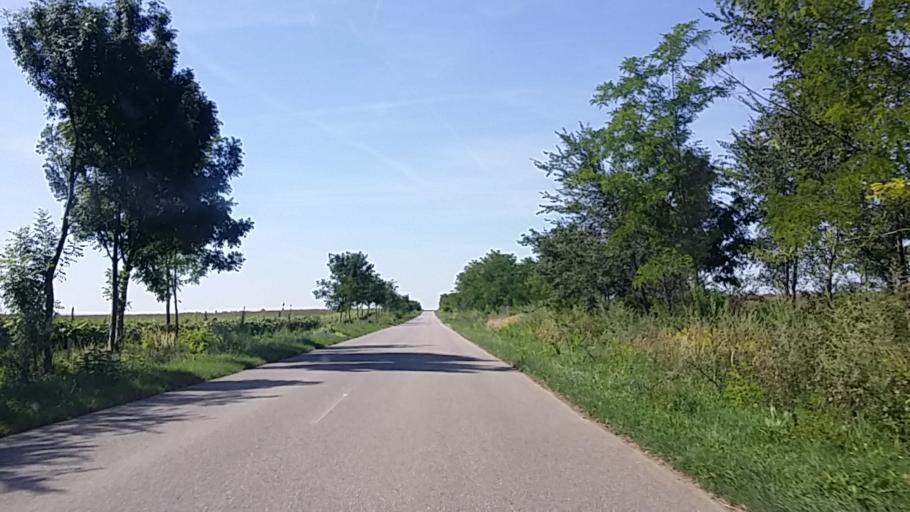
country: HU
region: Fejer
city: Deg
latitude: 46.8896
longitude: 18.4499
